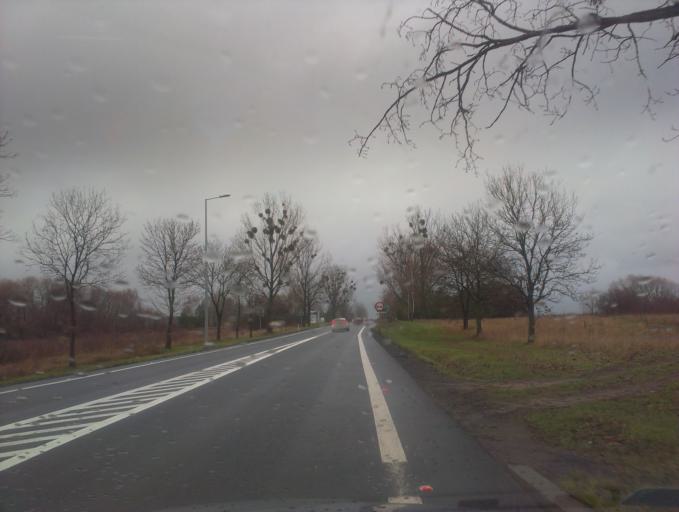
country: PL
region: Greater Poland Voivodeship
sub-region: Powiat poznanski
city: Zlotniki
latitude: 52.5364
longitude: 16.8363
